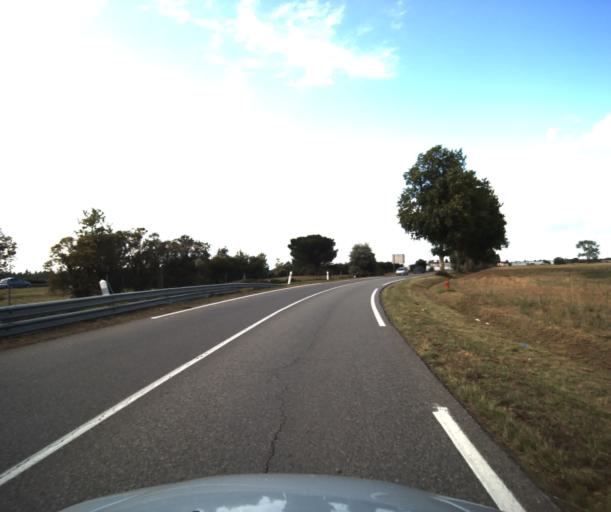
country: FR
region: Midi-Pyrenees
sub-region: Departement de la Haute-Garonne
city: Le Fauga
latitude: 43.4347
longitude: 1.3102
